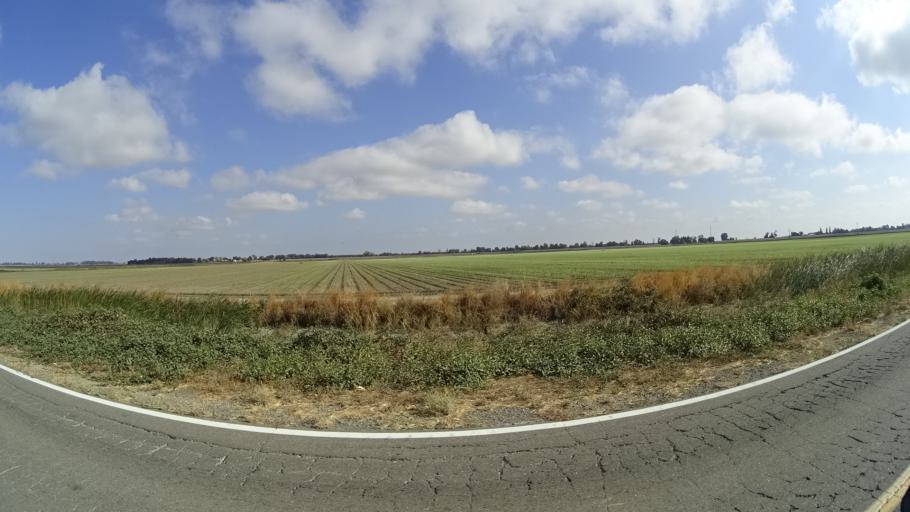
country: US
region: California
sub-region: Yolo County
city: Woodland
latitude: 38.8205
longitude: -121.7425
